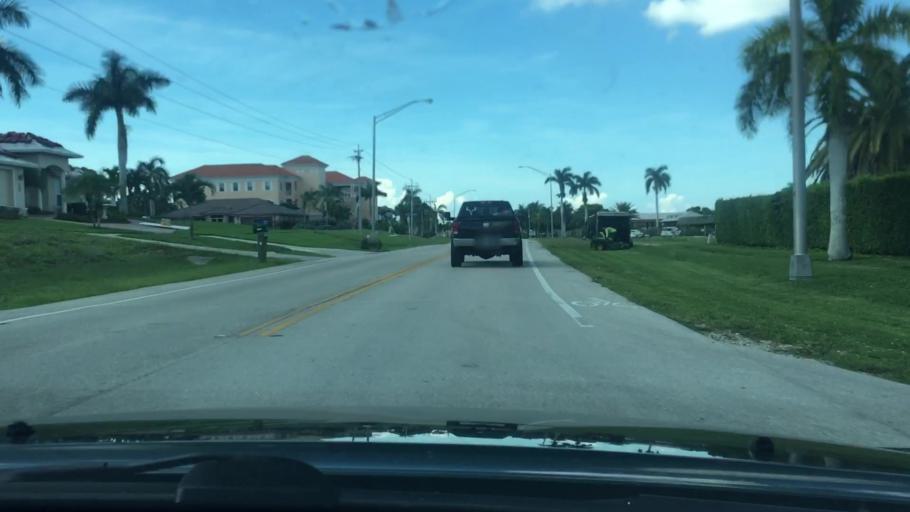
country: US
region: Florida
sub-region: Collier County
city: Marco
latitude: 25.9362
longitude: -81.6947
